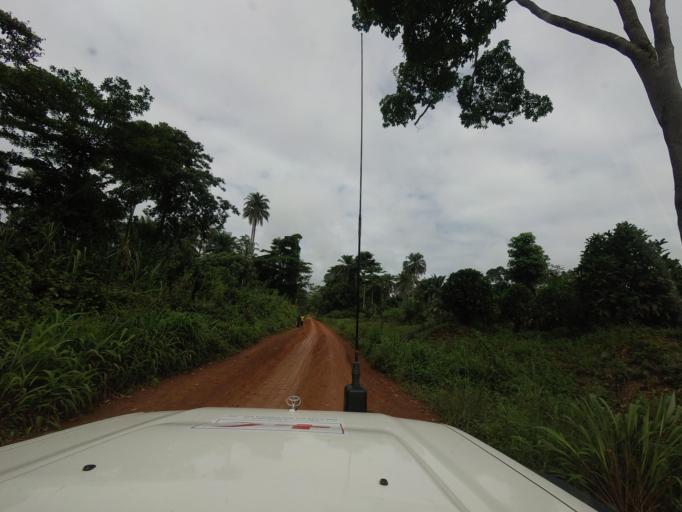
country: GN
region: Nzerekore
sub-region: Nzerekore Prefecture
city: Nzerekore
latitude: 7.7216
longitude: -8.8864
